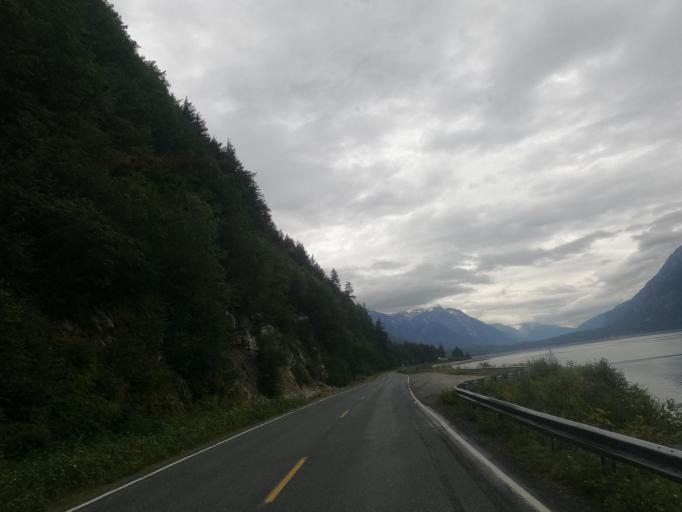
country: US
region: Alaska
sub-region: Haines Borough
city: Haines
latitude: 59.2927
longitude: -135.5005
